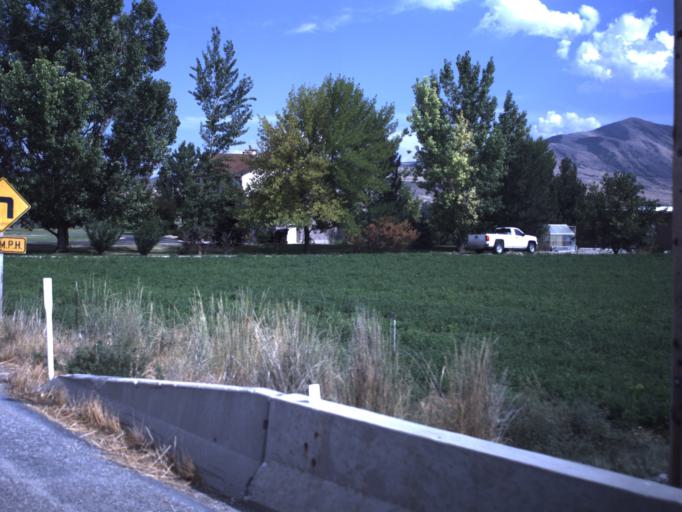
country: US
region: Utah
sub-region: Box Elder County
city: Garland
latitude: 41.7927
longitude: -112.1168
